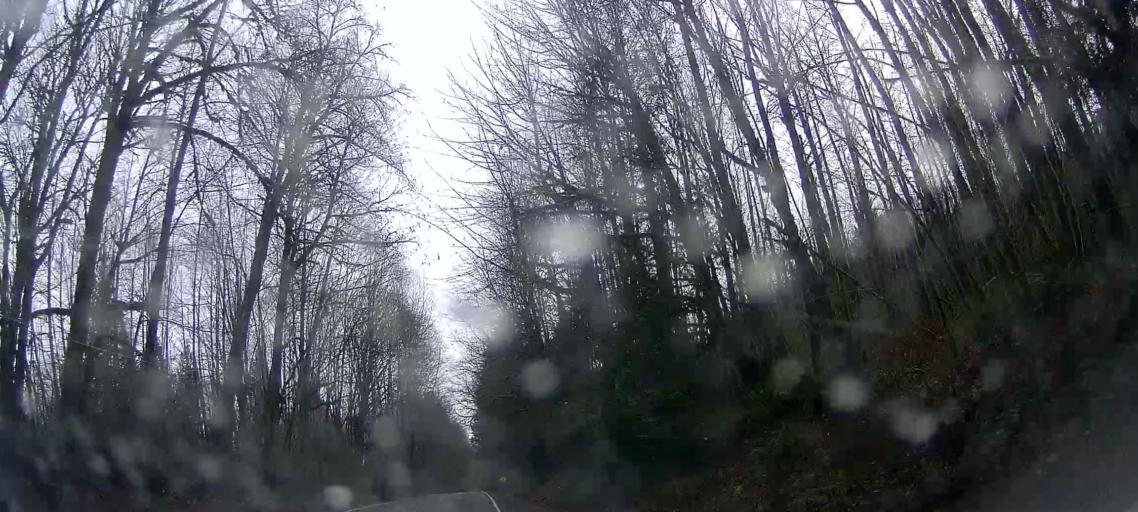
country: US
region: Washington
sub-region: Snohomish County
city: Darrington
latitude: 48.5304
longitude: -121.7861
